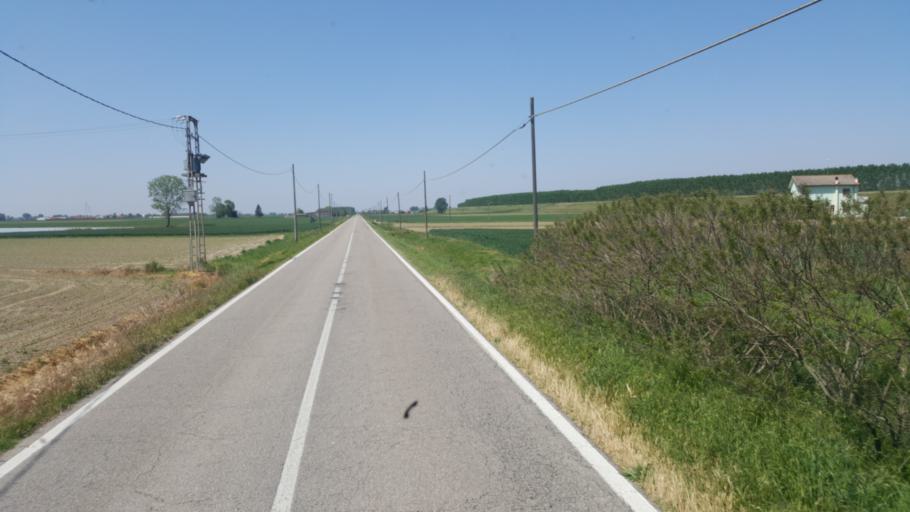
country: IT
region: Veneto
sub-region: Provincia di Rovigo
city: Salara
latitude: 44.9642
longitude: 11.4085
